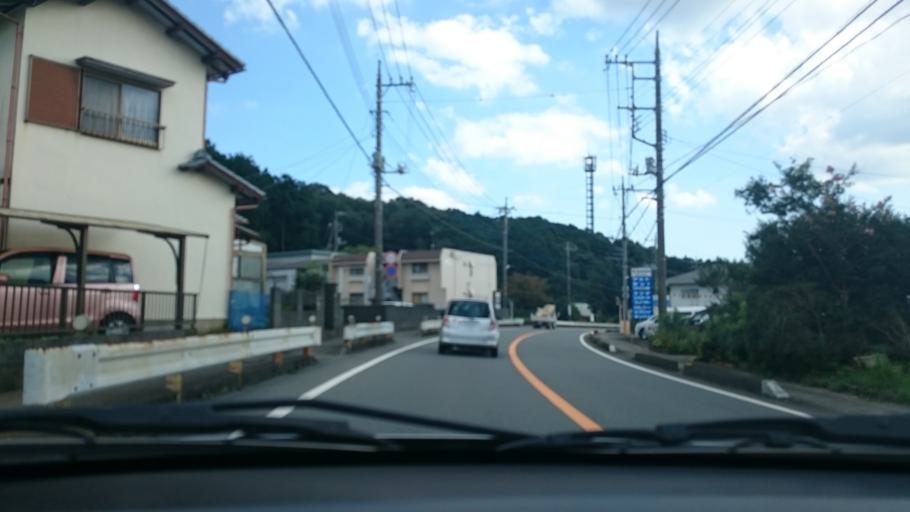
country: JP
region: Shizuoka
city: Gotemba
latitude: 35.2205
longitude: 138.9208
